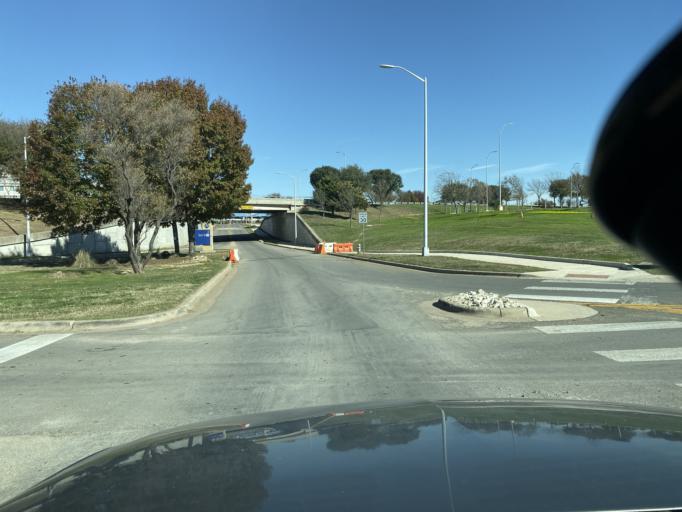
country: US
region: Texas
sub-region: Travis County
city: Hornsby Bend
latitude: 30.2093
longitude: -97.6651
